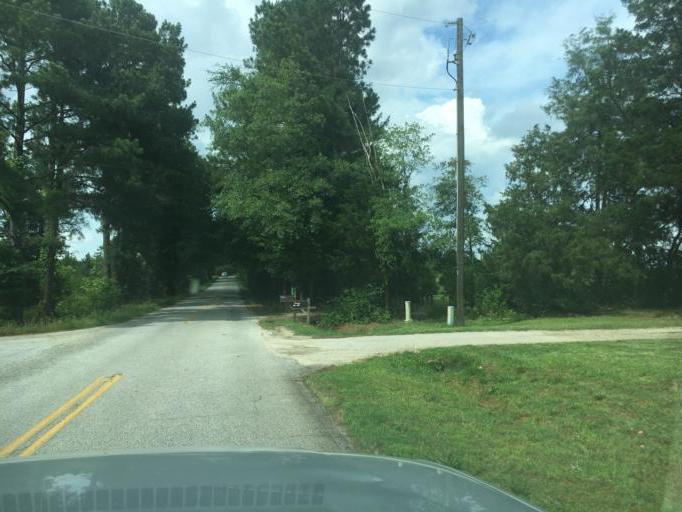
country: US
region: South Carolina
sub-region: Laurens County
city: Watts Mills
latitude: 34.5280
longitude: -81.9669
